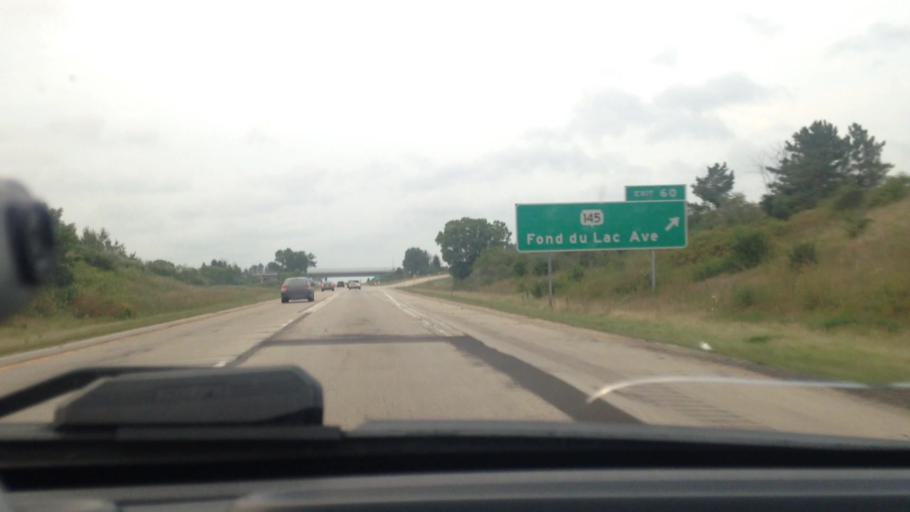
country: US
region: Wisconsin
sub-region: Washington County
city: Richfield
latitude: 43.2783
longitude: -88.1852
